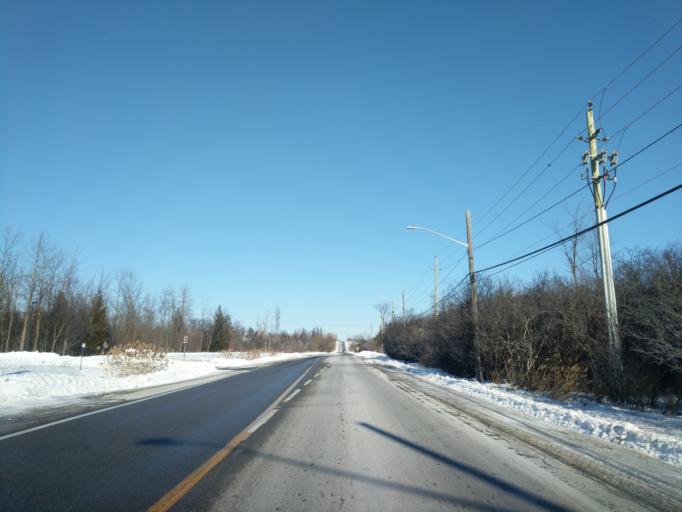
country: CA
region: Ontario
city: Pickering
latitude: 43.8440
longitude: -79.1267
